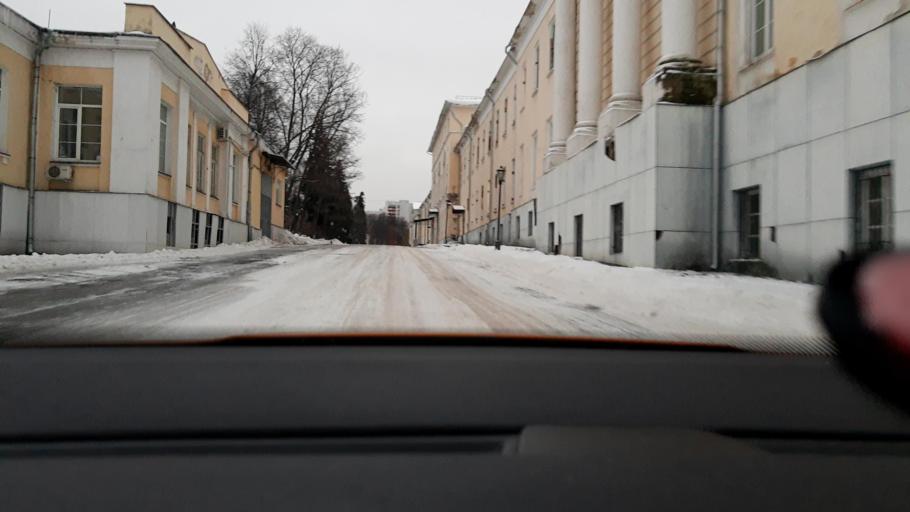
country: RU
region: Moscow
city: Lefortovo
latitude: 55.7696
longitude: 37.6957
